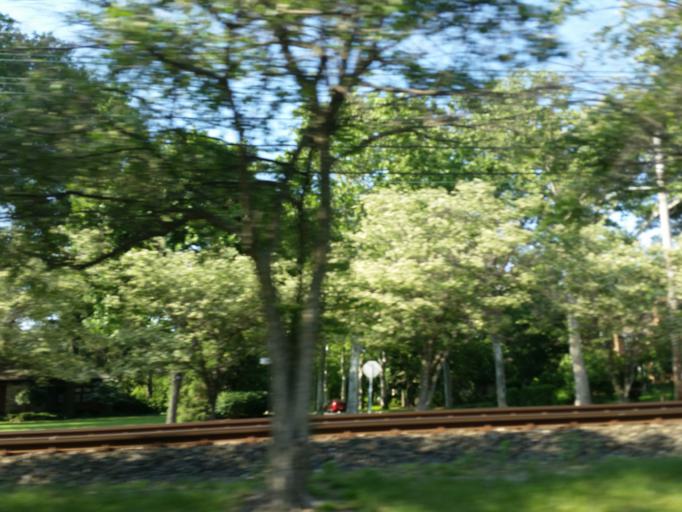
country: US
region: Ohio
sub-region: Cuyahoga County
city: Shaker Heights
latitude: 41.4827
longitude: -81.5810
